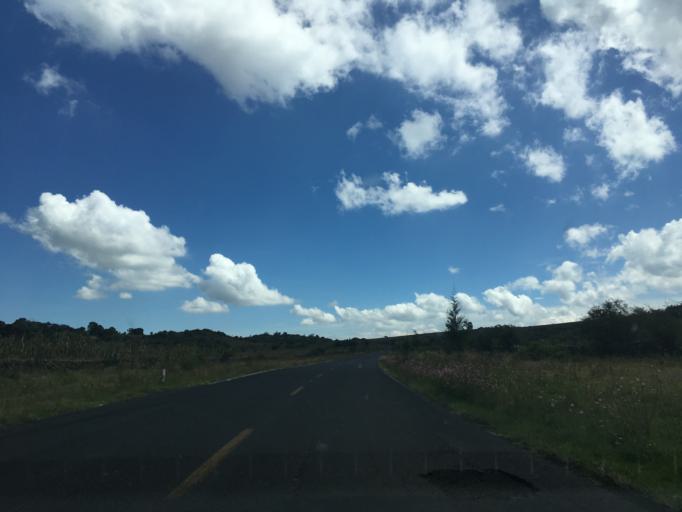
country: MX
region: Michoacan
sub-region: Morelia
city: Cuto de la Esperanza
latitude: 19.7725
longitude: -101.3889
